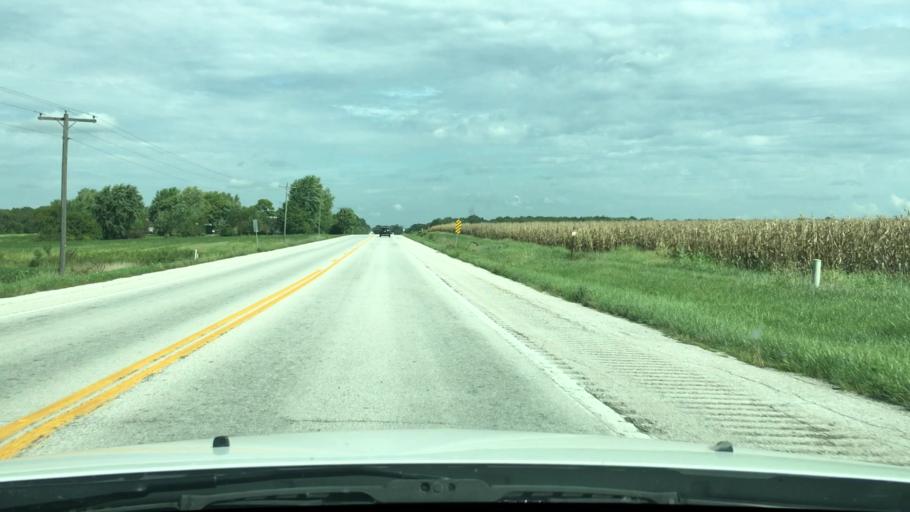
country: US
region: Missouri
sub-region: Montgomery County
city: Wellsville
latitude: 39.1927
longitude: -91.6468
